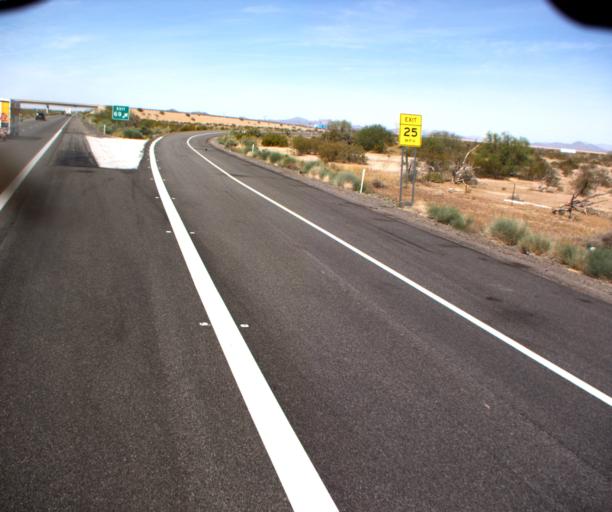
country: US
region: Arizona
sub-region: La Paz County
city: Salome
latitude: 33.5686
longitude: -113.3480
